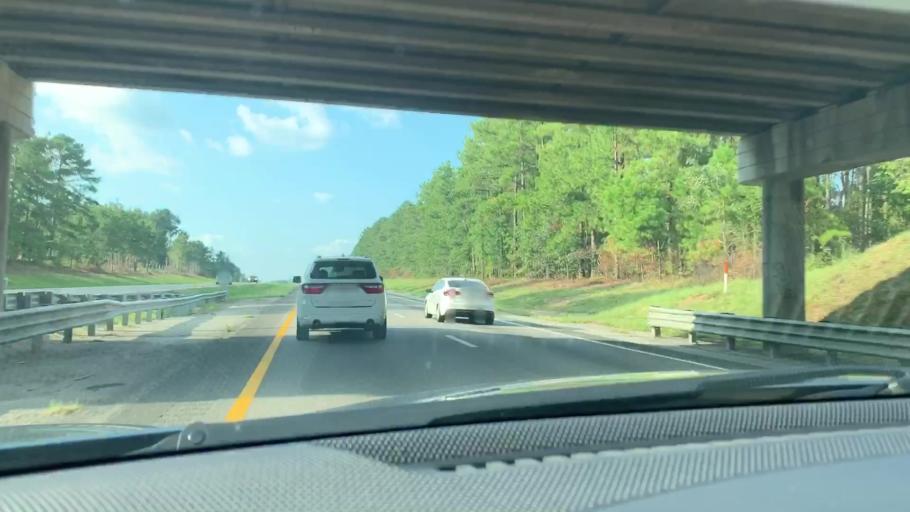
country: US
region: South Carolina
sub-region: Calhoun County
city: Oak Grove
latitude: 33.7004
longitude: -80.9151
